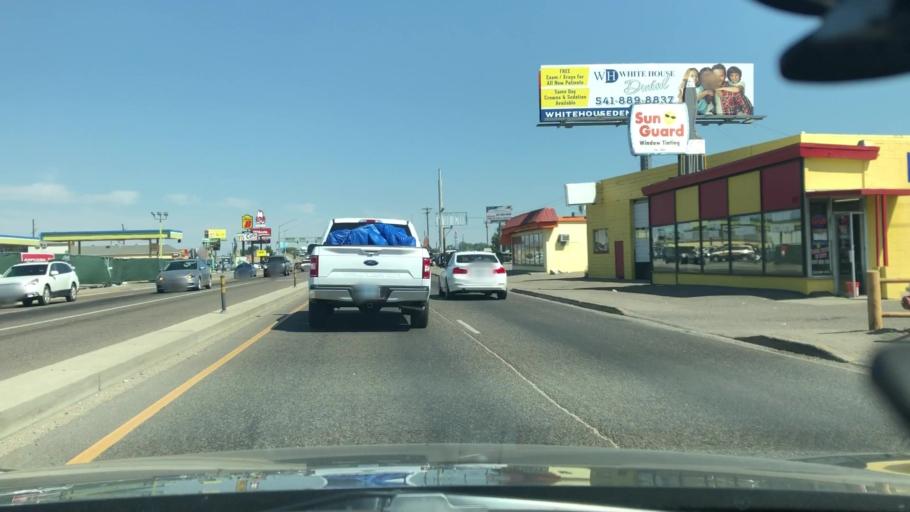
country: US
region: Oregon
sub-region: Malheur County
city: Ontario
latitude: 44.0254
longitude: -116.9556
